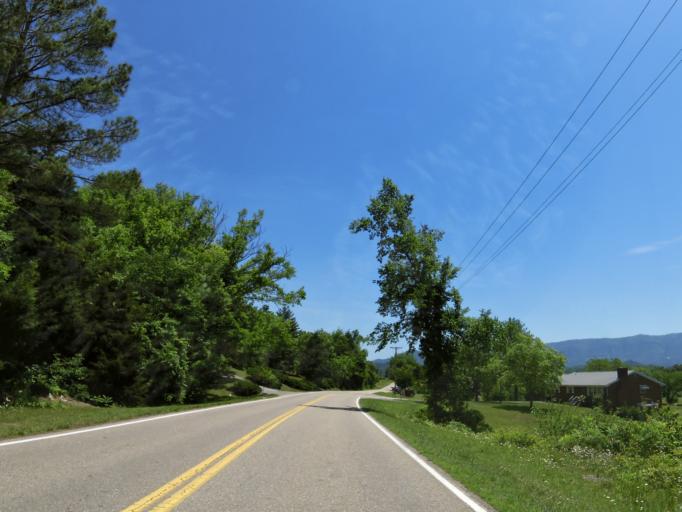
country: US
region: Tennessee
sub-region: Jefferson County
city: Dandridge
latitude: 35.9624
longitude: -83.3816
